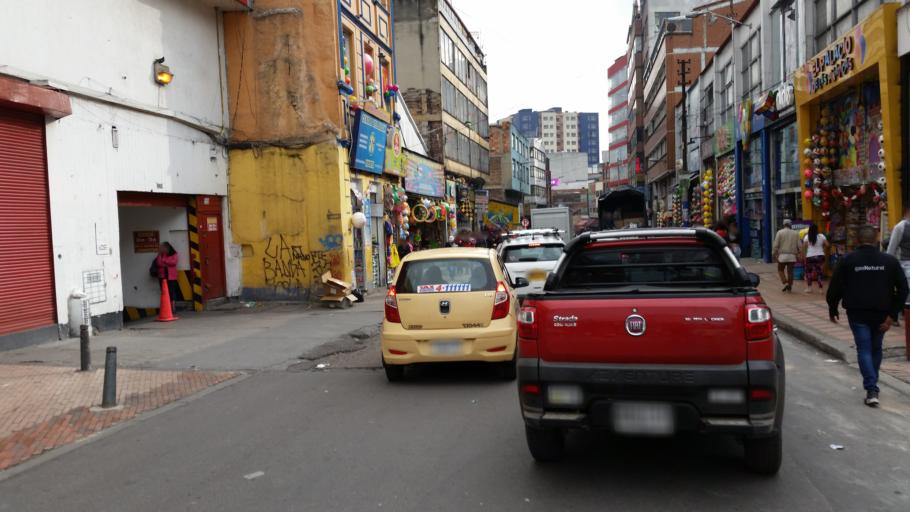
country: CO
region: Bogota D.C.
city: Bogota
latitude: 4.6020
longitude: -74.0793
